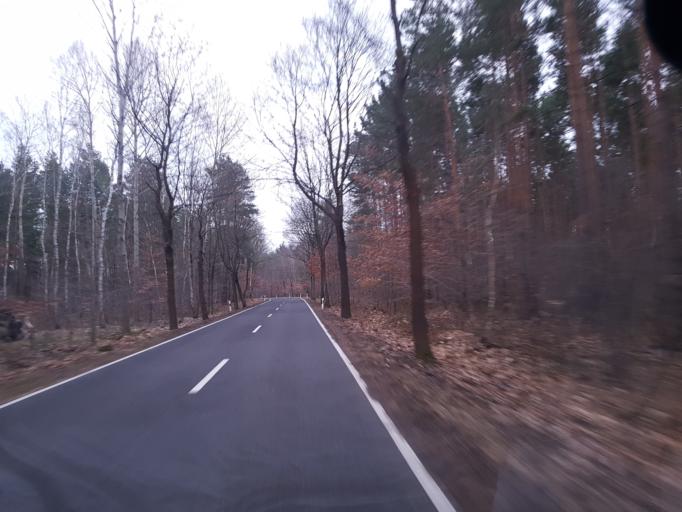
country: DE
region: Brandenburg
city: Sallgast
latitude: 51.5757
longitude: 13.8525
